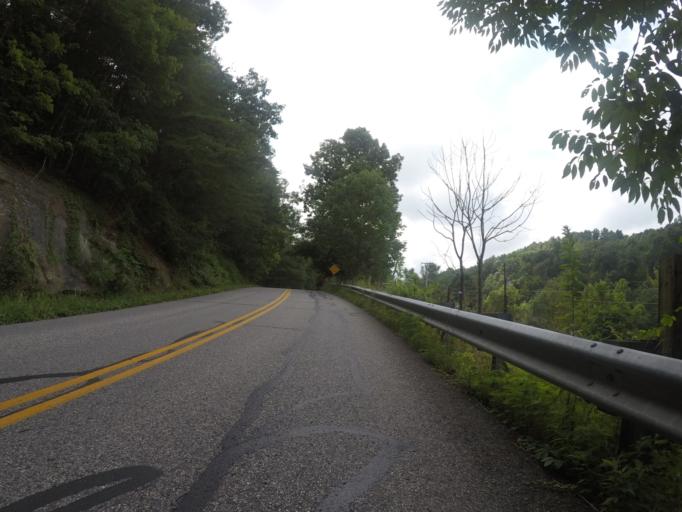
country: US
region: Kentucky
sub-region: Boyd County
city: Meads
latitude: 38.4094
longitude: -82.6679
